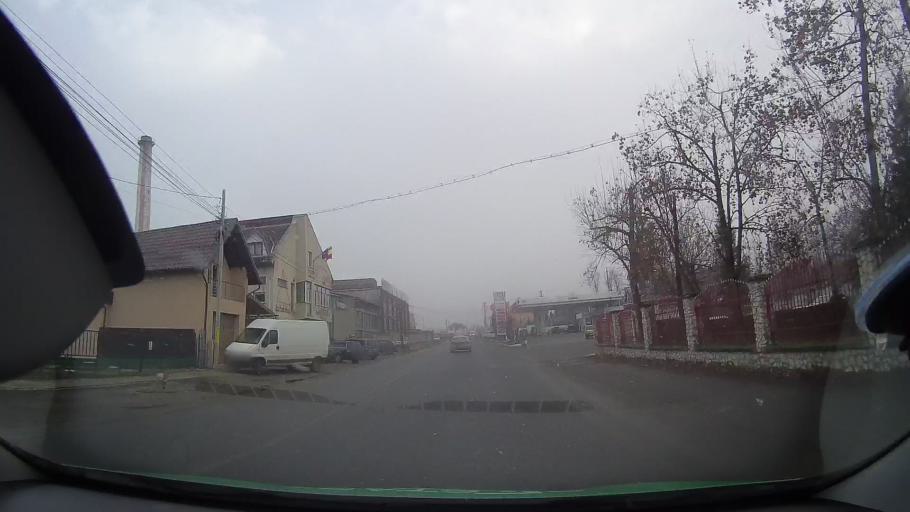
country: RO
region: Mures
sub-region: Municipiul Tarnaveni
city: Tarnaveni
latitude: 46.3164
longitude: 24.2971
